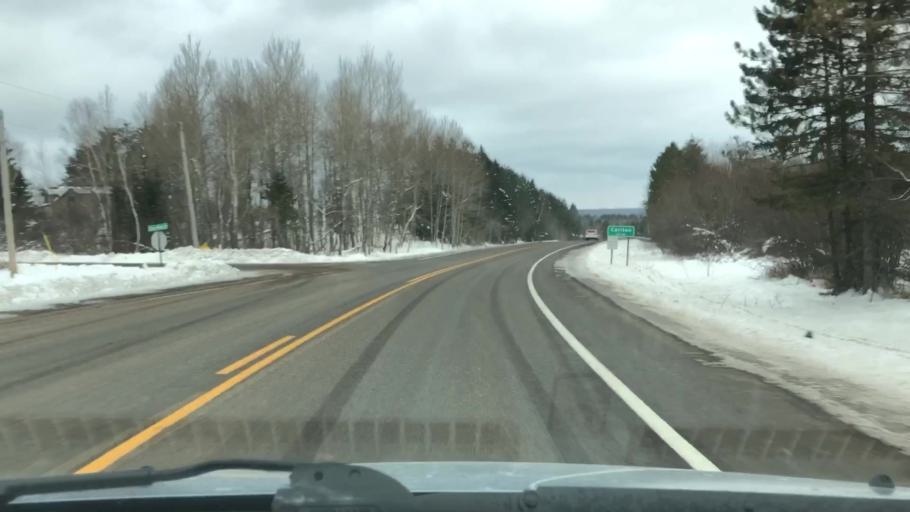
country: US
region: Minnesota
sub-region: Carlton County
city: Esko
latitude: 46.6773
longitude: -92.3748
